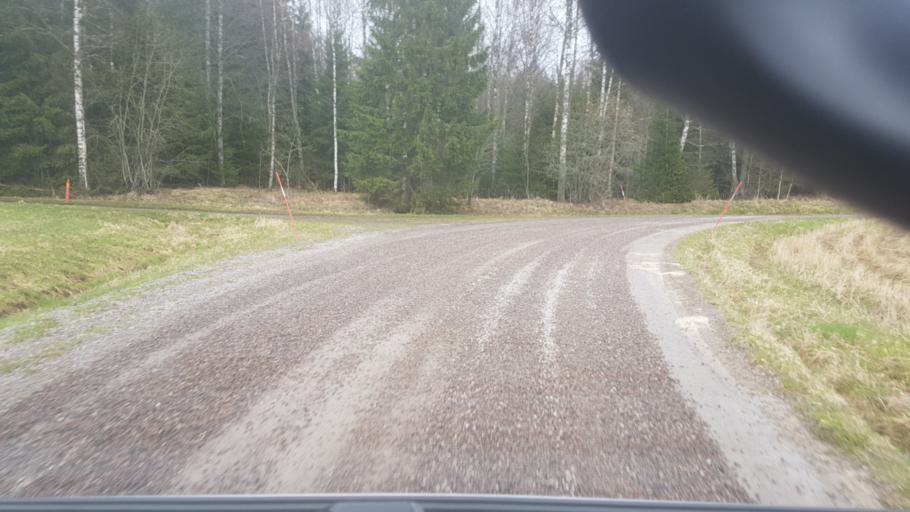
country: SE
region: Vaermland
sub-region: Eda Kommun
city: Charlottenberg
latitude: 59.8379
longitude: 12.3557
